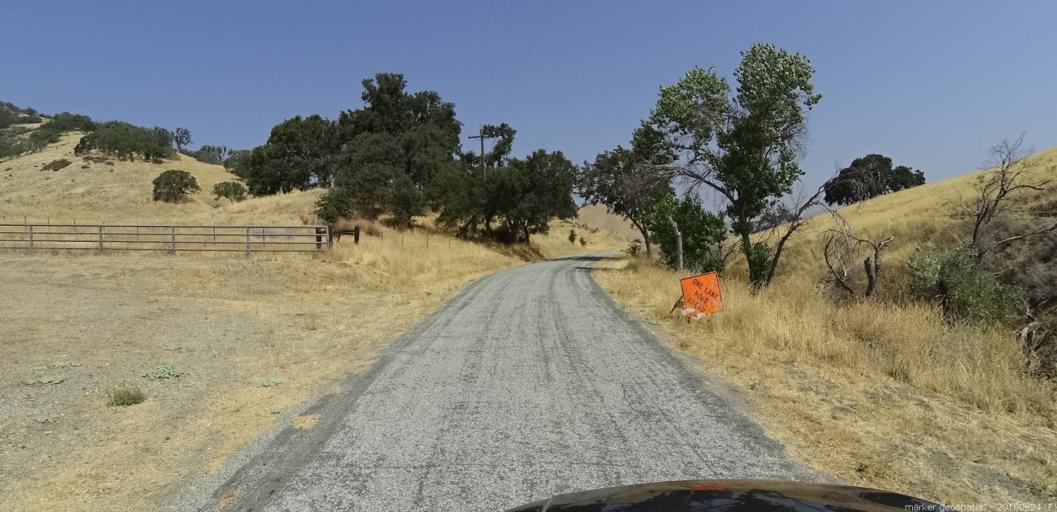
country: US
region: California
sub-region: San Luis Obispo County
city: San Miguel
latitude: 35.9944
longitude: -120.6468
